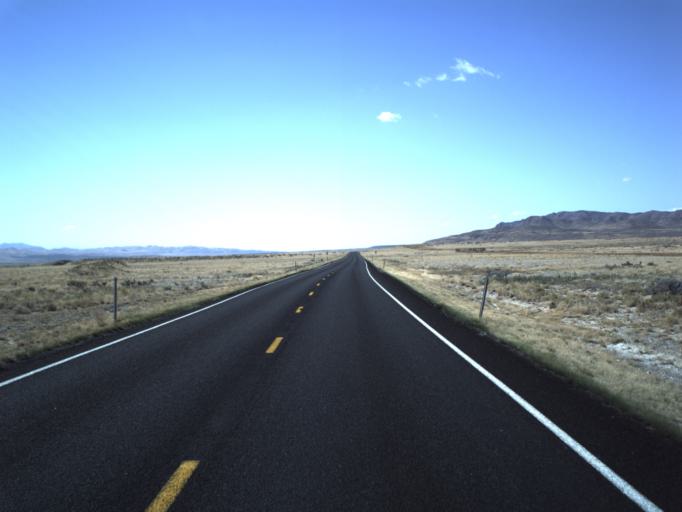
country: US
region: Utah
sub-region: Millard County
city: Fillmore
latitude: 38.9177
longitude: -112.8130
